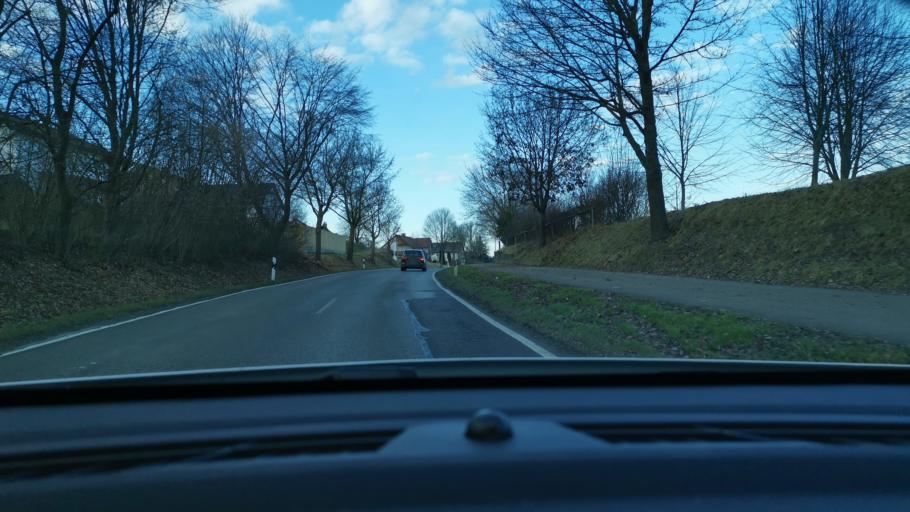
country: DE
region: Bavaria
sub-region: Swabia
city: Holzheim
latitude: 48.5853
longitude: 10.9617
